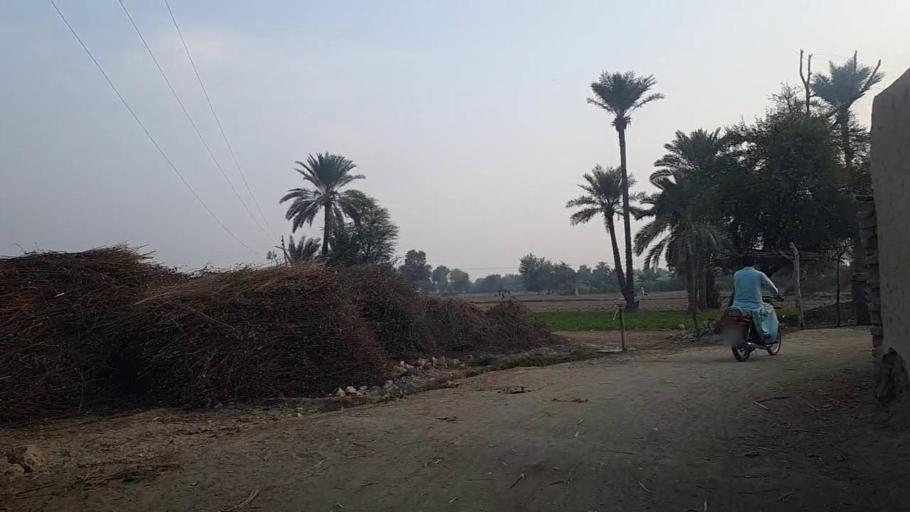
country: PK
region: Sindh
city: Kot Diji
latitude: 27.3754
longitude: 68.6661
